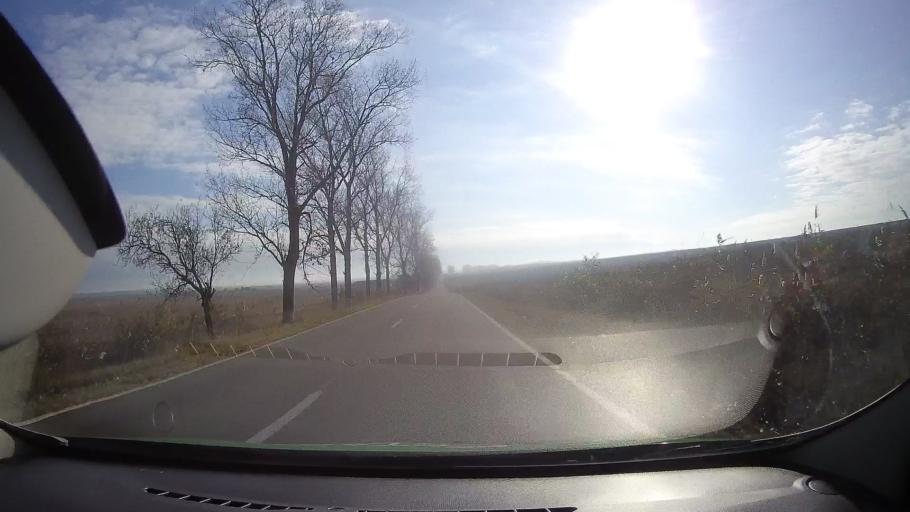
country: RO
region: Tulcea
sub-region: Comuna Mahmudia
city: Mahmudia
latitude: 45.0653
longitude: 29.1081
